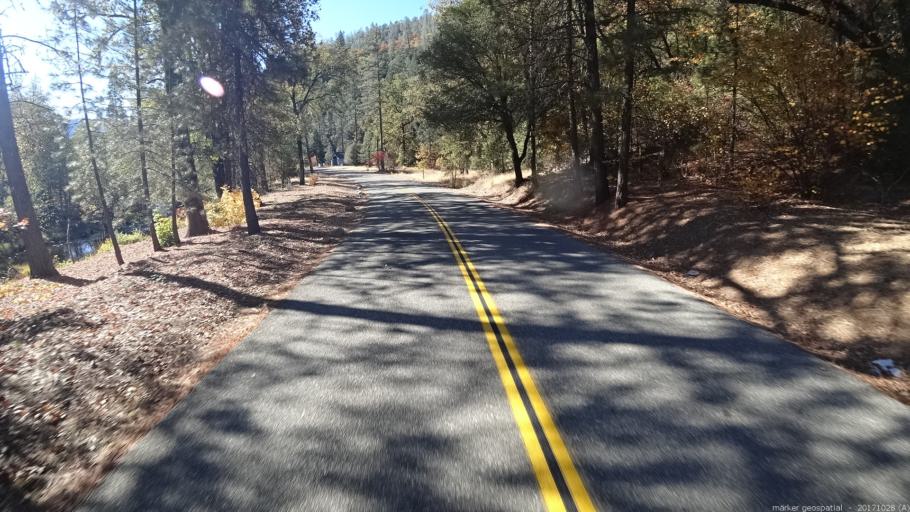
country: US
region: California
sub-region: Trinity County
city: Lewiston
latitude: 40.7842
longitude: -122.6130
